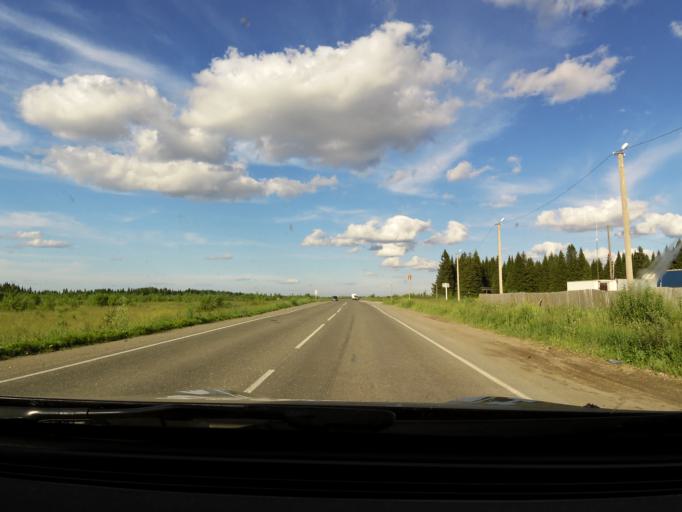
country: RU
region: Kirov
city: Omutninsk
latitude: 58.6885
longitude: 52.1620
